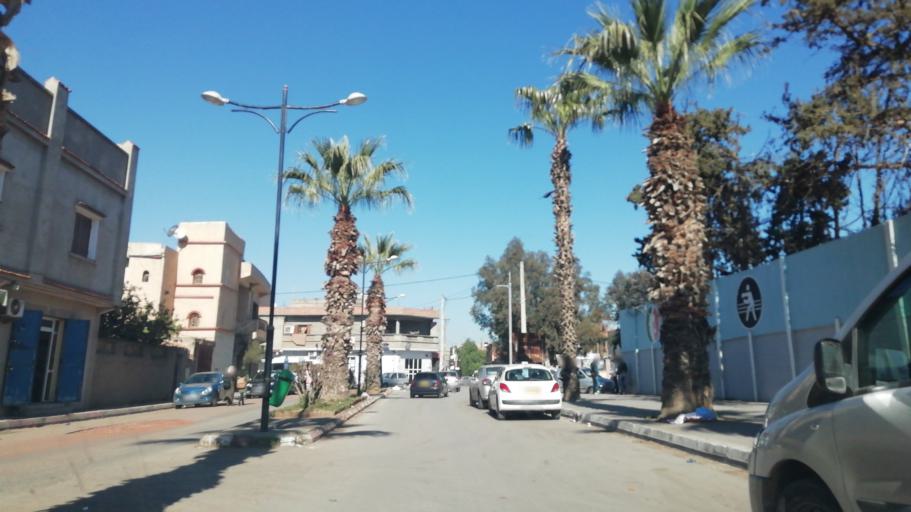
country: DZ
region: Oran
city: Es Senia
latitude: 35.6518
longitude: -0.6220
